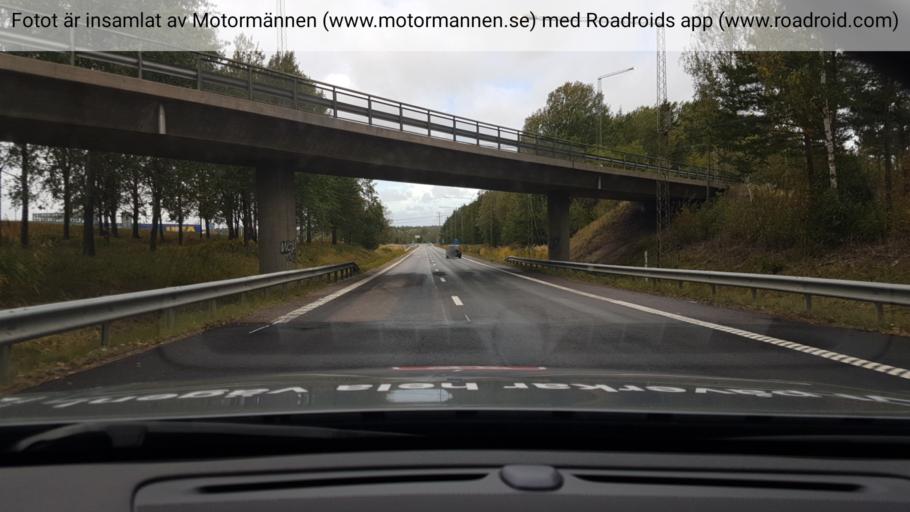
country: SE
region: Vaermland
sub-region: Hammaro Kommun
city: Skoghall
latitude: 59.3794
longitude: 13.4293
